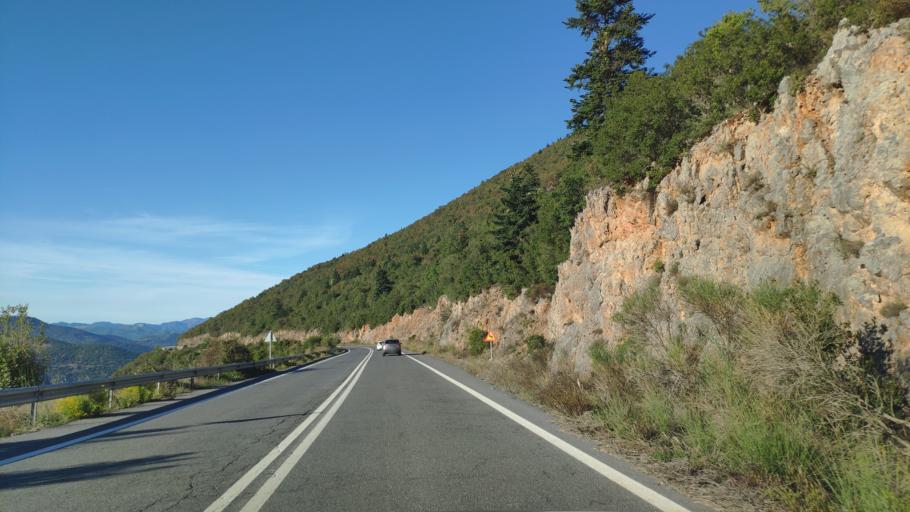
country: GR
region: Peloponnese
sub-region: Nomos Arkadias
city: Langadhia
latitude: 37.7023
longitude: 22.1976
